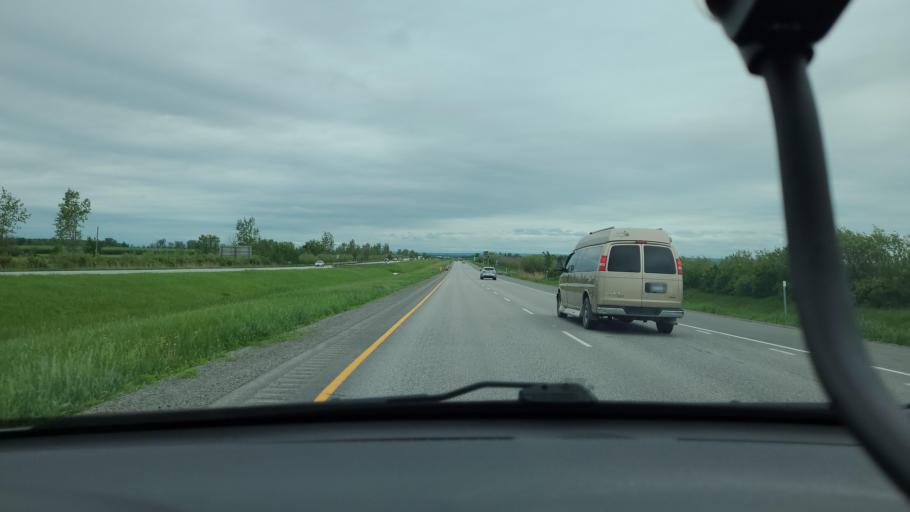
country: CA
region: Quebec
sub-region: Lanaudiere
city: Mascouche
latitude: 45.8450
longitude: -73.6311
